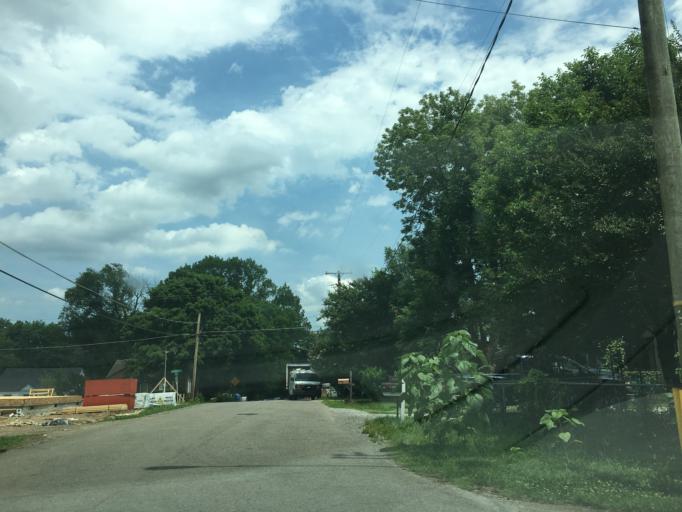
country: US
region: Tennessee
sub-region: Davidson County
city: Oak Hill
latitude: 36.1268
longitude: -86.7509
